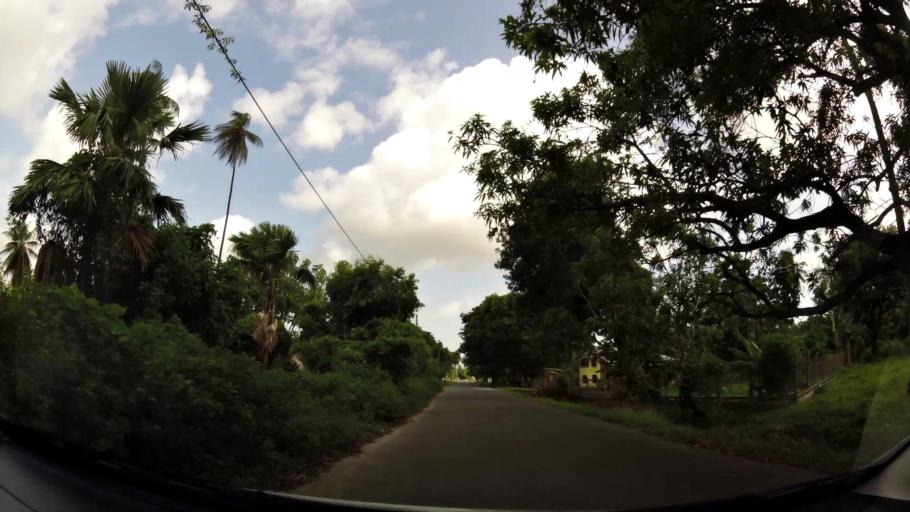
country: GY
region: Demerara-Mahaica
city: Mahaica Village
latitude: 6.7114
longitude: -57.9286
